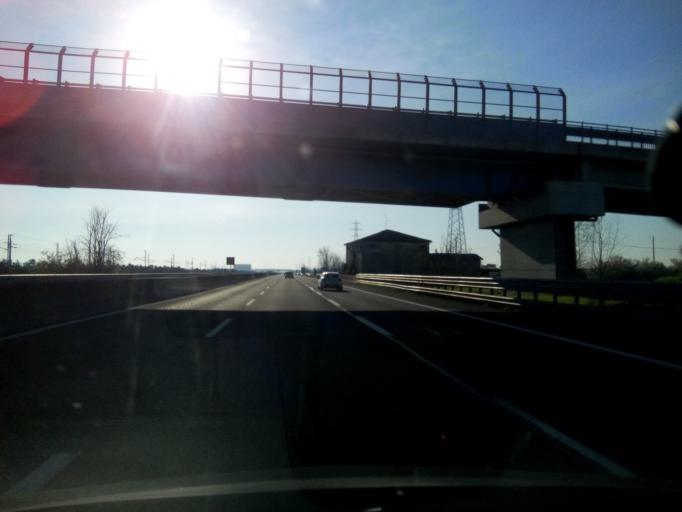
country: IT
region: Emilia-Romagna
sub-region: Provincia di Reggio Emilia
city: Prato
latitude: 44.7024
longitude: 10.7440
